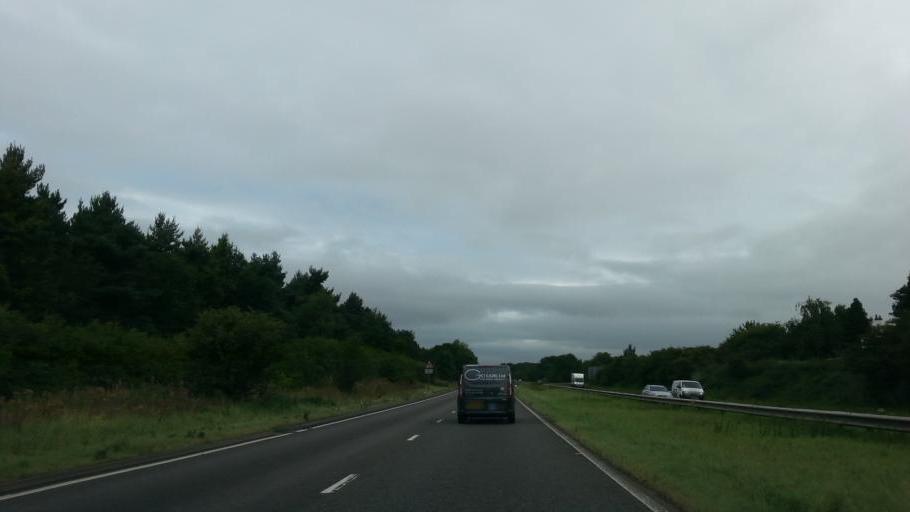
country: GB
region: England
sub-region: Nottinghamshire
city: Babworth
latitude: 53.3226
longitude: -1.0277
